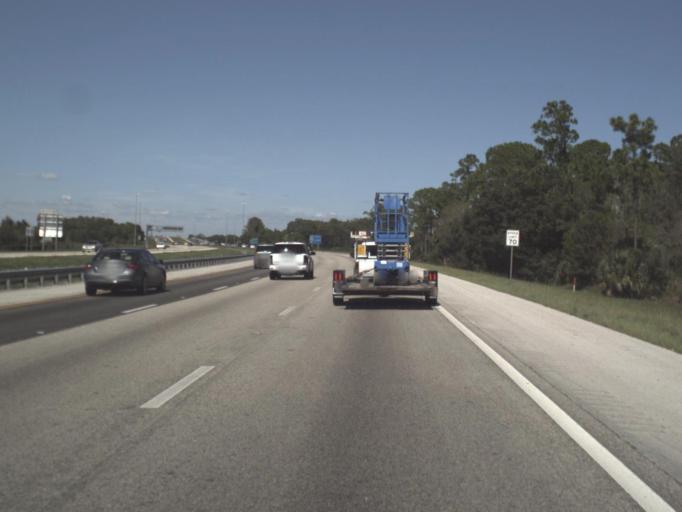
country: US
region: Florida
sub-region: Lee County
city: Tice
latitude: 26.6455
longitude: -81.7995
